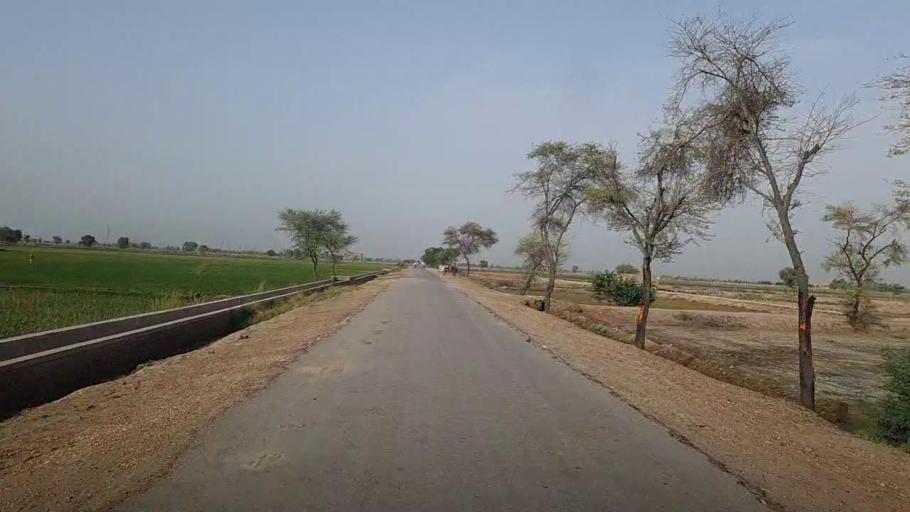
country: PK
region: Sindh
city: Mehar
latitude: 27.1675
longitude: 67.8165
